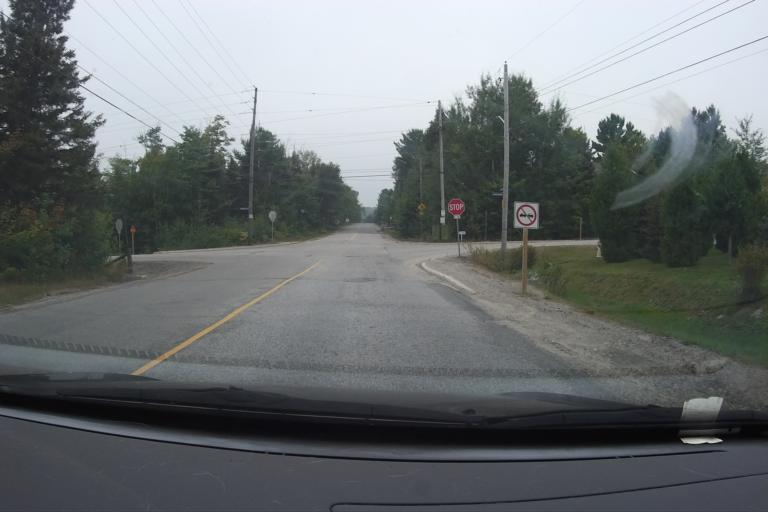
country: CA
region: Ontario
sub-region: Nipissing District
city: North Bay
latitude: 46.3470
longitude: -79.4866
